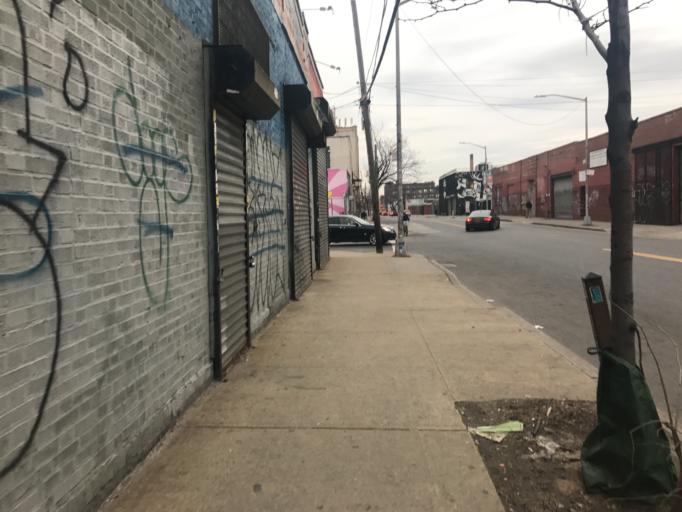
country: US
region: New York
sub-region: Queens County
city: Long Island City
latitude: 40.7097
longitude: -73.9333
